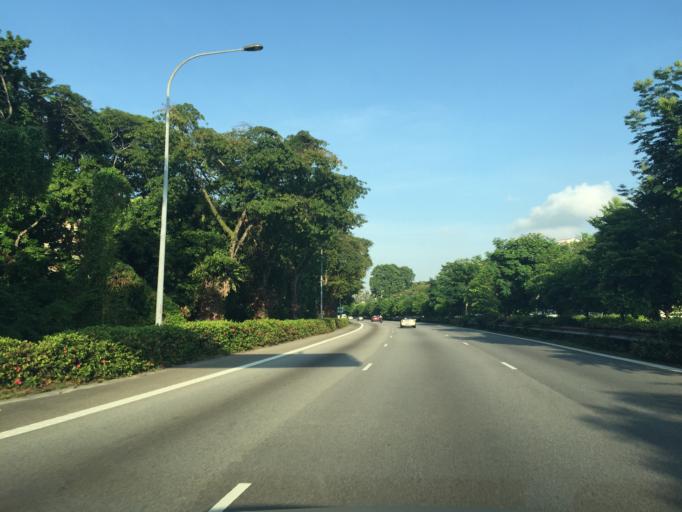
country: SG
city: Singapore
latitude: 1.3505
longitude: 103.9603
